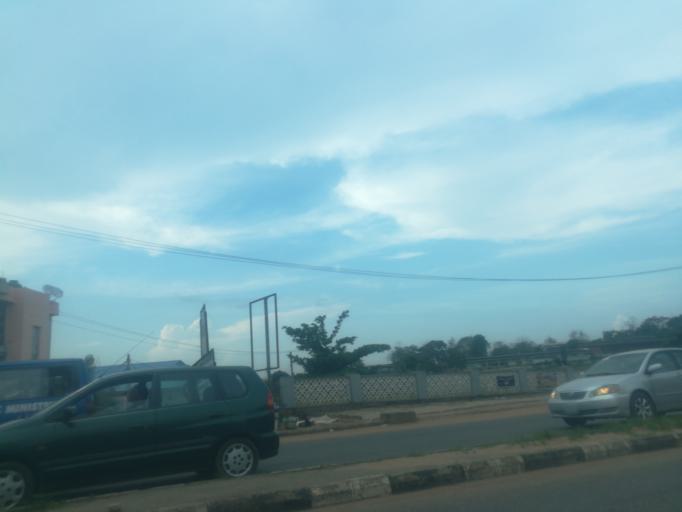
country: NG
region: Oyo
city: Ibadan
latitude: 7.4269
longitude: 3.9011
